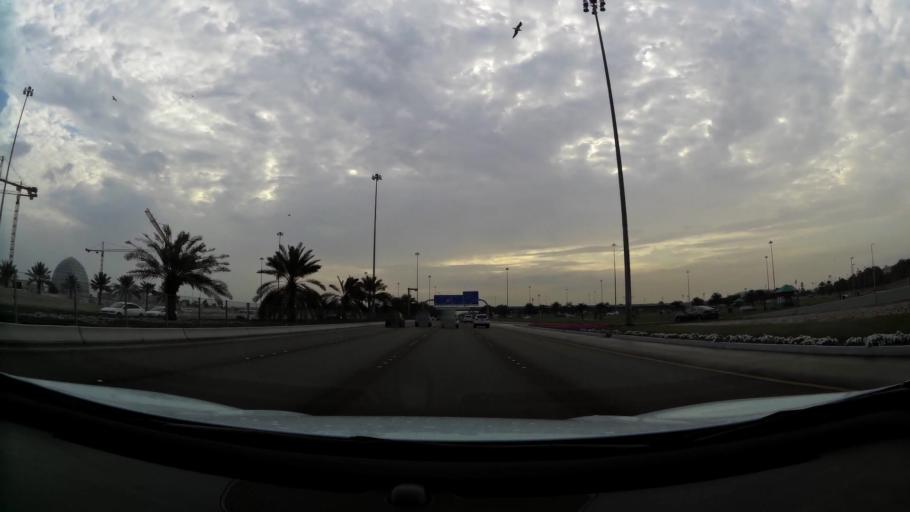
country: AE
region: Abu Dhabi
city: Abu Dhabi
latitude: 24.4068
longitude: 54.4735
